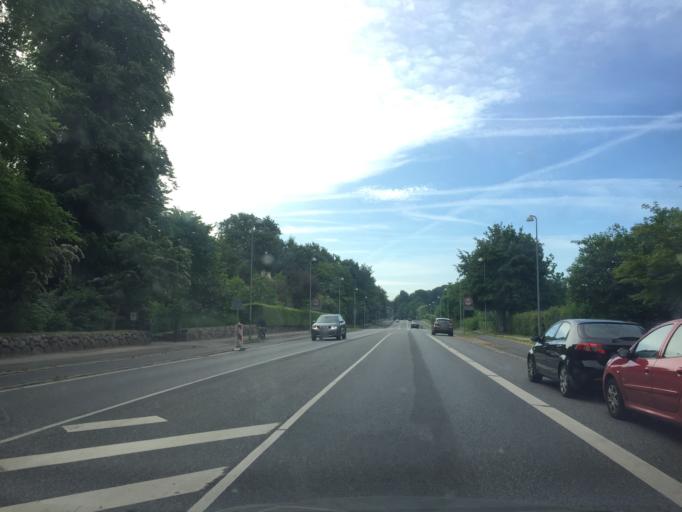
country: DK
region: Capital Region
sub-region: Lyngby-Tarbaek Kommune
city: Kongens Lyngby
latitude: 55.7830
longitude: 12.4912
